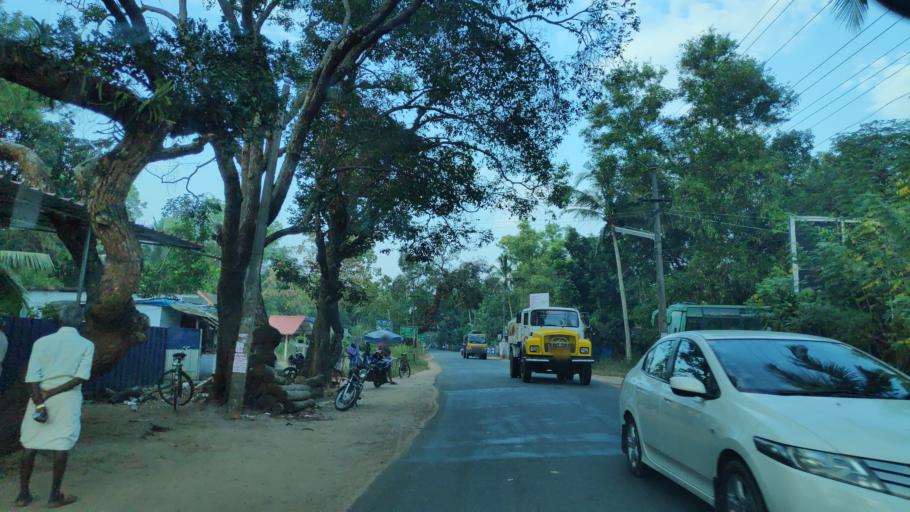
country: IN
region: Kerala
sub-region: Alappuzha
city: Shertallai
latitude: 9.6340
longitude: 76.3712
